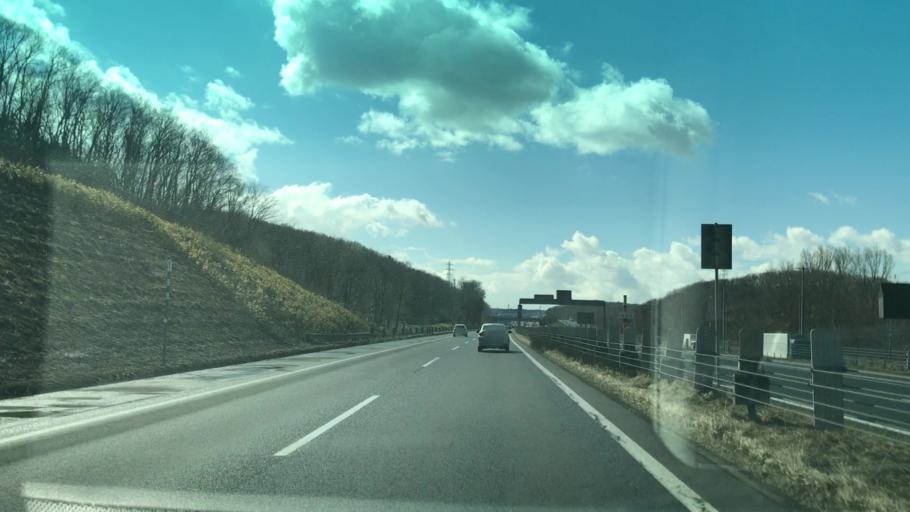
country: JP
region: Hokkaido
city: Kitahiroshima
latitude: 43.0074
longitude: 141.4667
